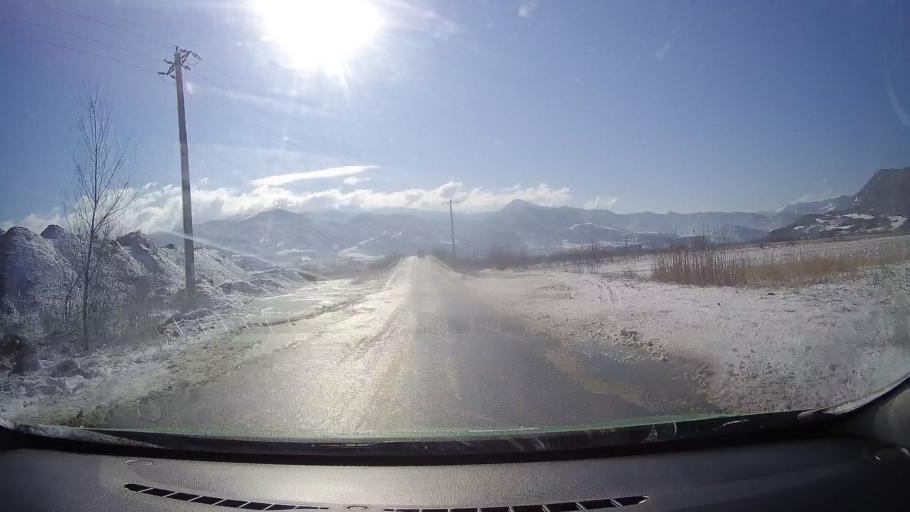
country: RO
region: Sibiu
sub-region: Comuna Turnu Rosu
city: Turnu Rosu
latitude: 45.6567
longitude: 24.2972
